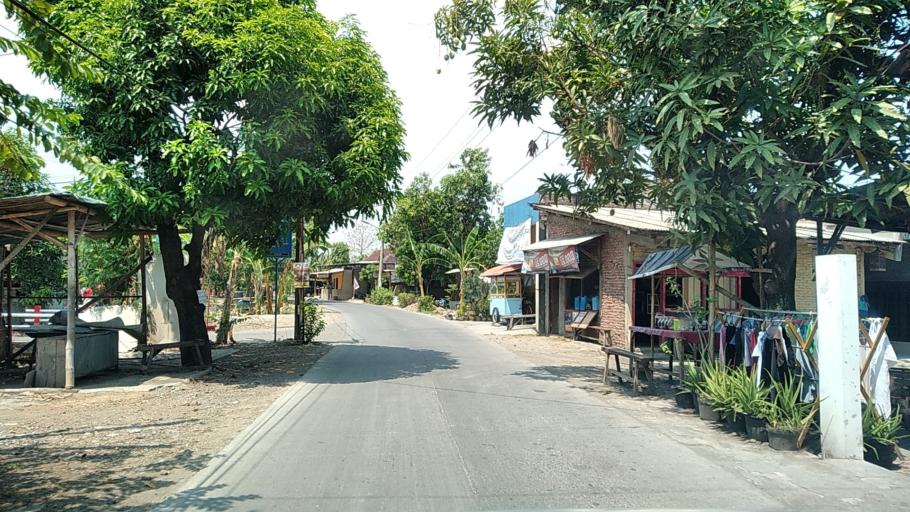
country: ID
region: Central Java
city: Mranggen
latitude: -7.0199
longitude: 110.4816
